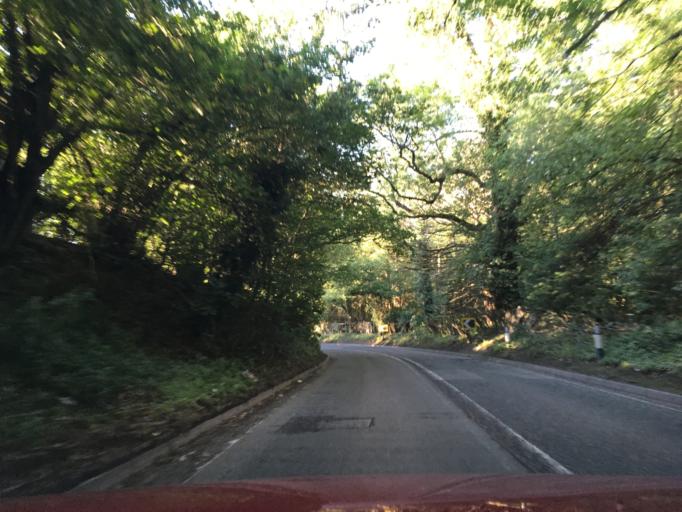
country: GB
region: England
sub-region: Hampshire
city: Tadley
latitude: 51.3749
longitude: -1.1510
